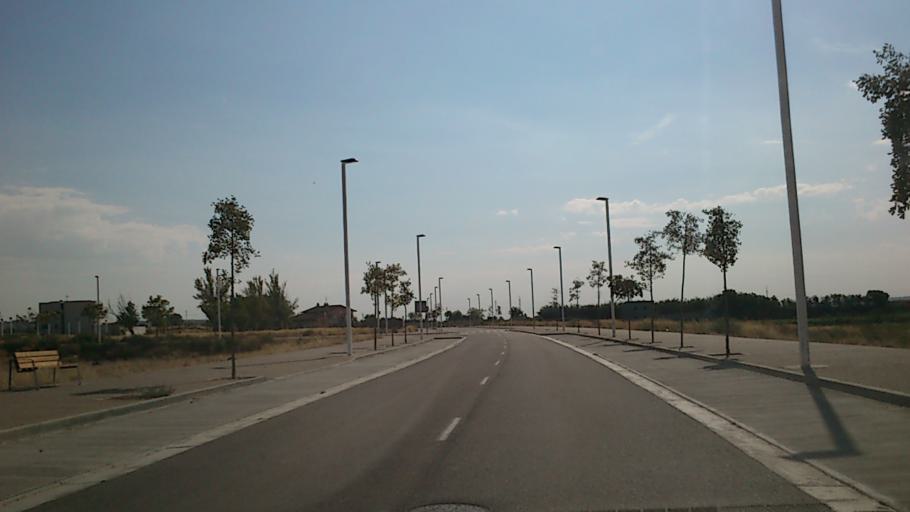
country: ES
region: Aragon
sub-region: Provincia de Zaragoza
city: Puebla de Alfinden
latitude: 41.6298
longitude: -0.7565
